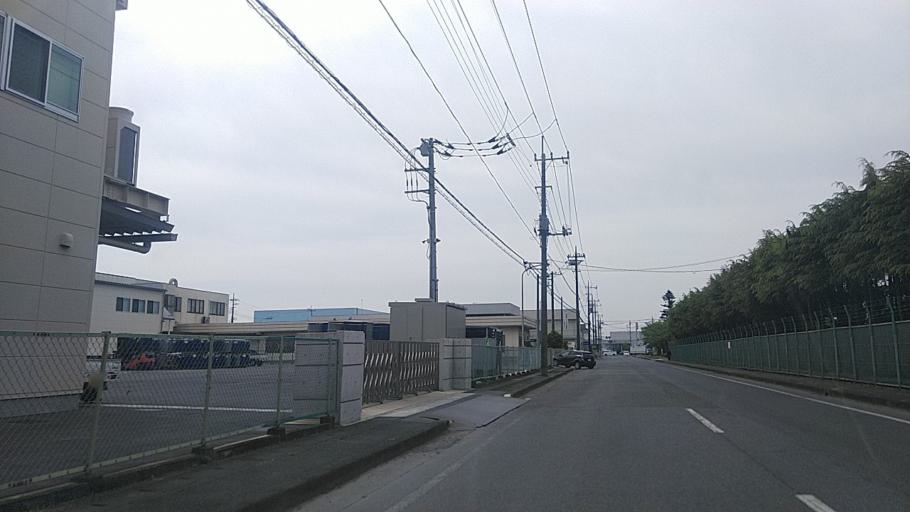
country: JP
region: Gunma
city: Ota
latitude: 36.2726
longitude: 139.3430
